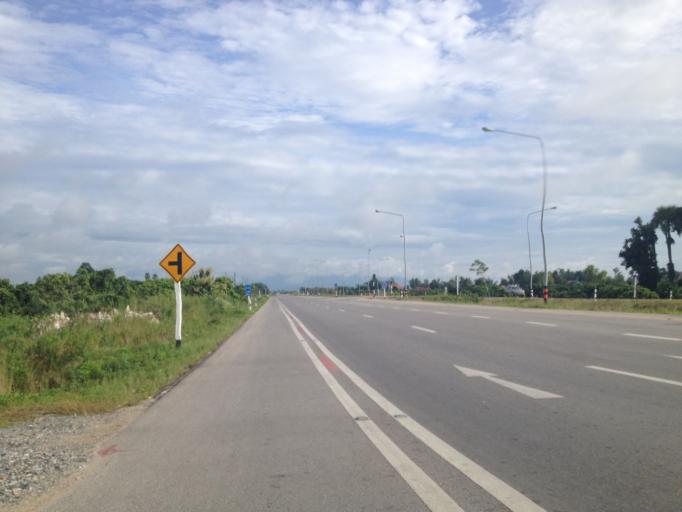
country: TH
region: Chiang Mai
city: San Pa Tong
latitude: 18.5504
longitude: 98.8489
